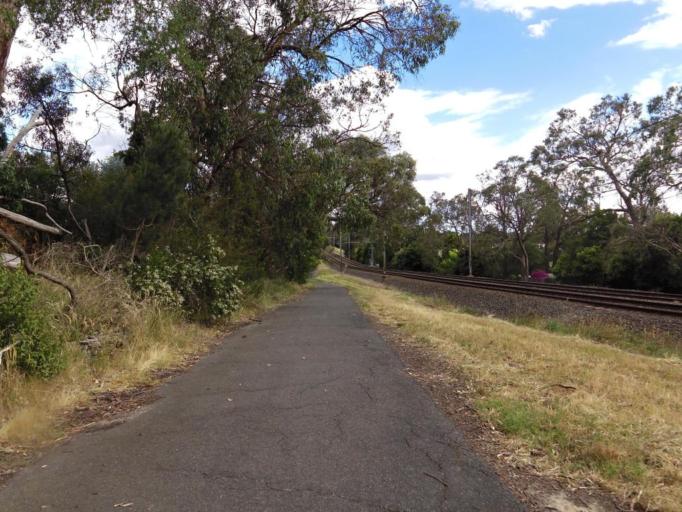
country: AU
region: Victoria
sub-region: Maroondah
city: Ringwood East
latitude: -37.8213
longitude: 145.2409
